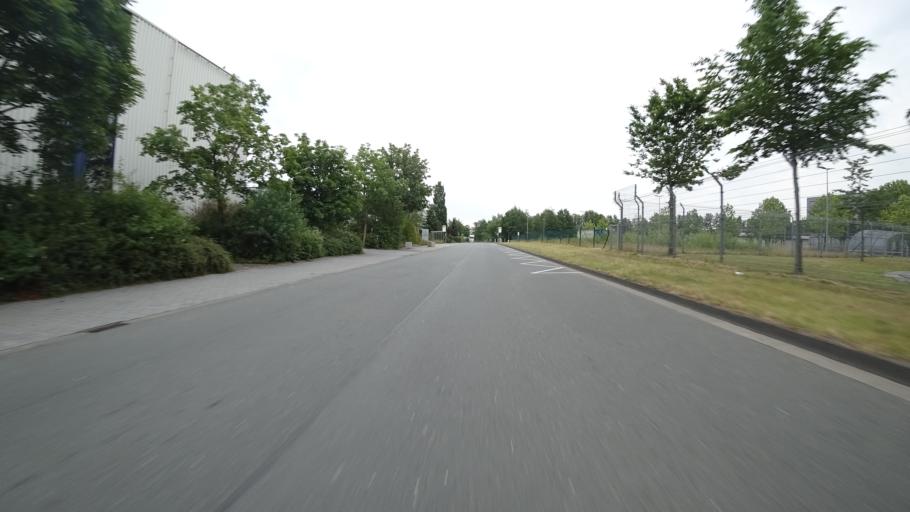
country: DE
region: North Rhine-Westphalia
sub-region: Regierungsbezirk Detmold
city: Verl
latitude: 51.8856
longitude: 8.4479
